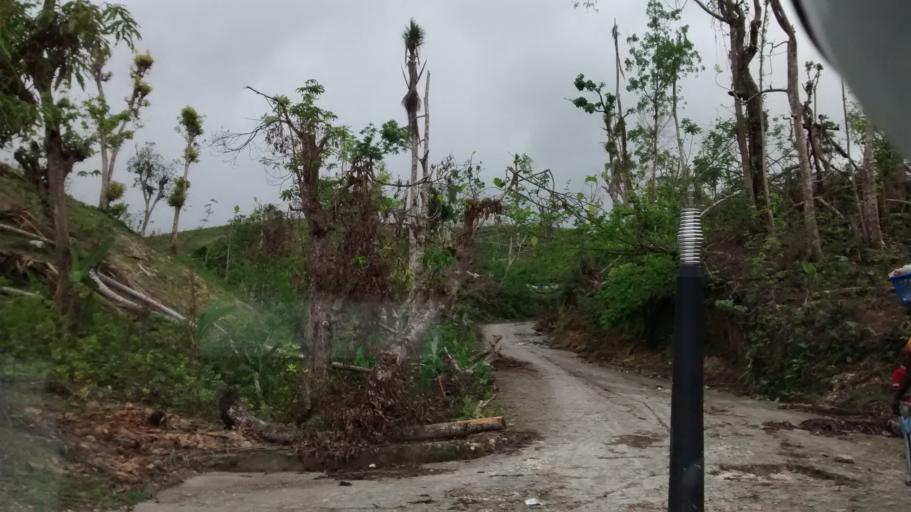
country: HT
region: Grandans
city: Jeremie
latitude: 18.5649
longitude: -74.1527
